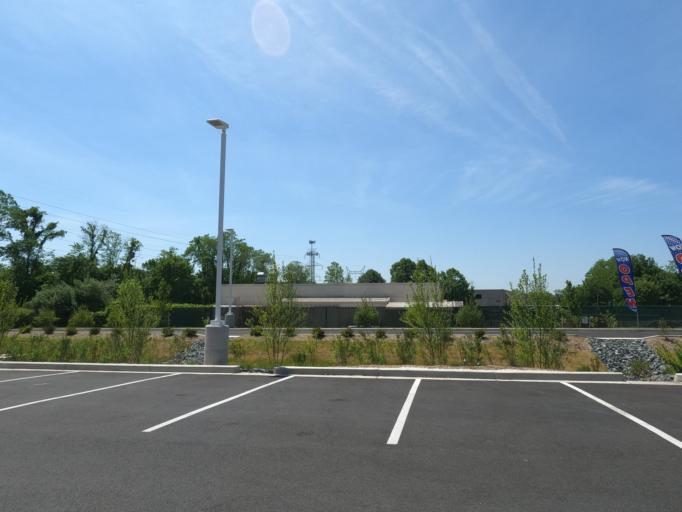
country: US
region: Maryland
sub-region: Howard County
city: Riverside
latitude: 39.1758
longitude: -76.8446
